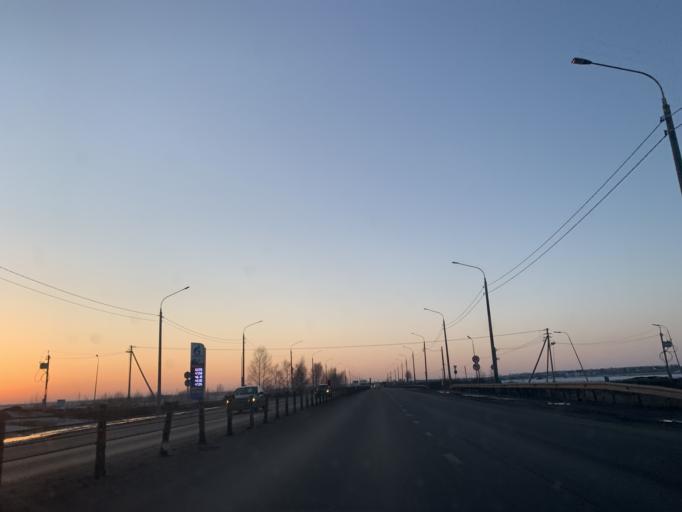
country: RU
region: Jaroslavl
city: Yaroslavl
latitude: 57.6207
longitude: 39.7732
